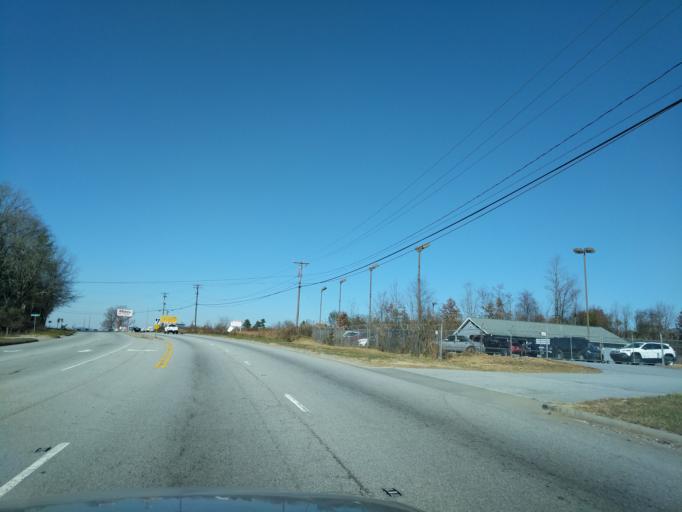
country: US
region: North Carolina
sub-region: Henderson County
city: Fletcher
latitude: 35.4027
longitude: -82.5095
